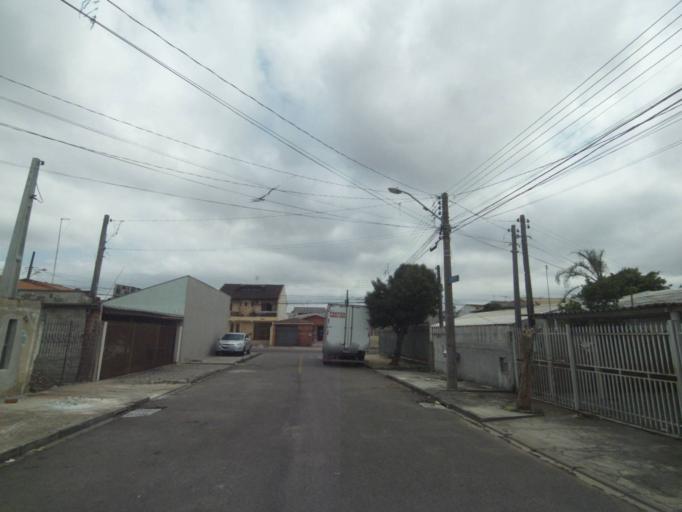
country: BR
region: Parana
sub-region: Sao Jose Dos Pinhais
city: Sao Jose dos Pinhais
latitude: -25.5468
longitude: -49.2544
